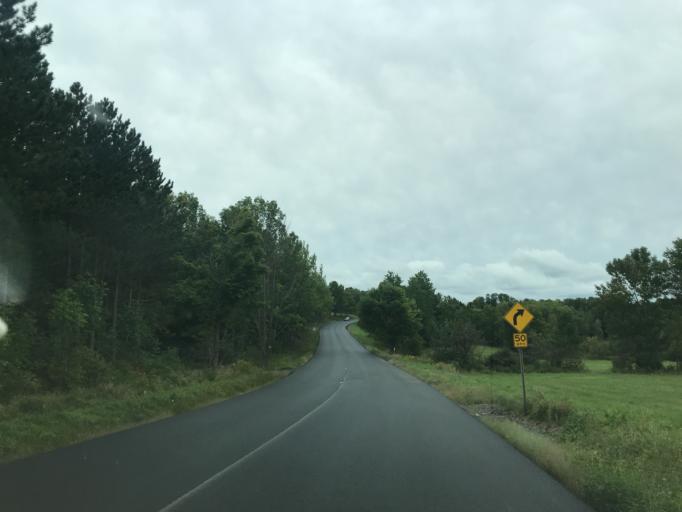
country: US
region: New York
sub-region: Delaware County
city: Stamford
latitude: 42.5176
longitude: -74.6255
